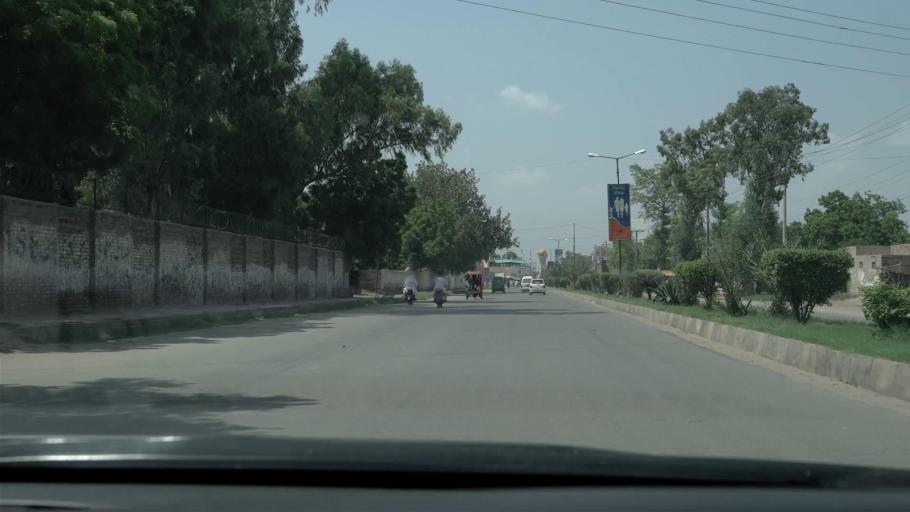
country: PK
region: Punjab
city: Gojra
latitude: 31.1537
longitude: 72.6710
